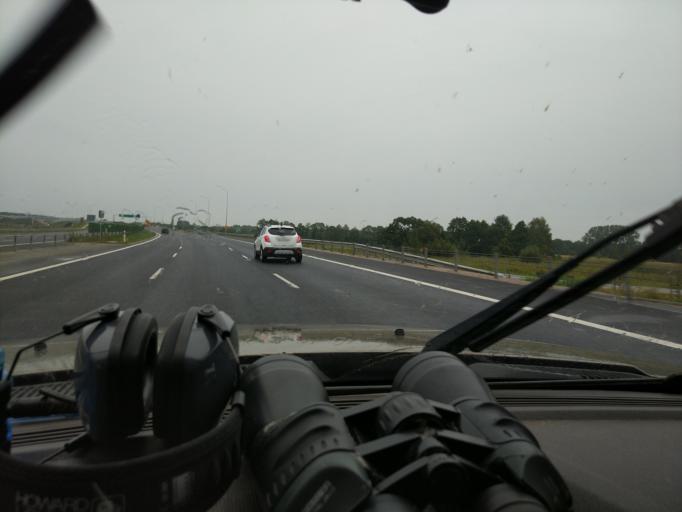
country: PL
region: Masovian Voivodeship
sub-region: Powiat wolominski
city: Kobylka
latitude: 52.3642
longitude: 21.1890
